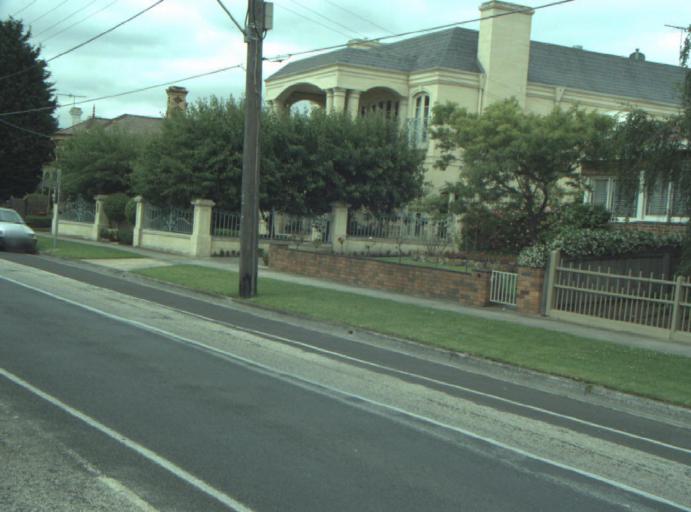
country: AU
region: Victoria
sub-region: Greater Geelong
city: Geelong West
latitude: -38.1391
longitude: 144.3561
